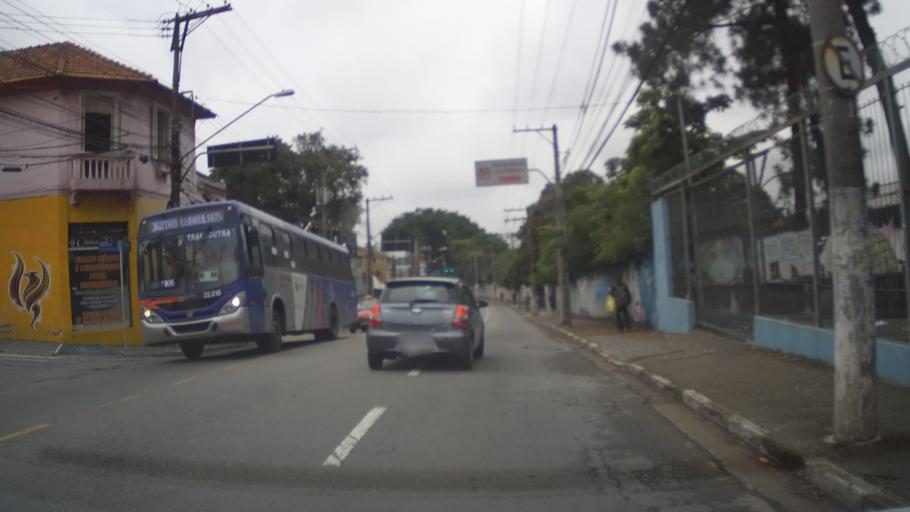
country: BR
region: Sao Paulo
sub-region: Guarulhos
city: Guarulhos
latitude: -23.4689
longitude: -46.5173
